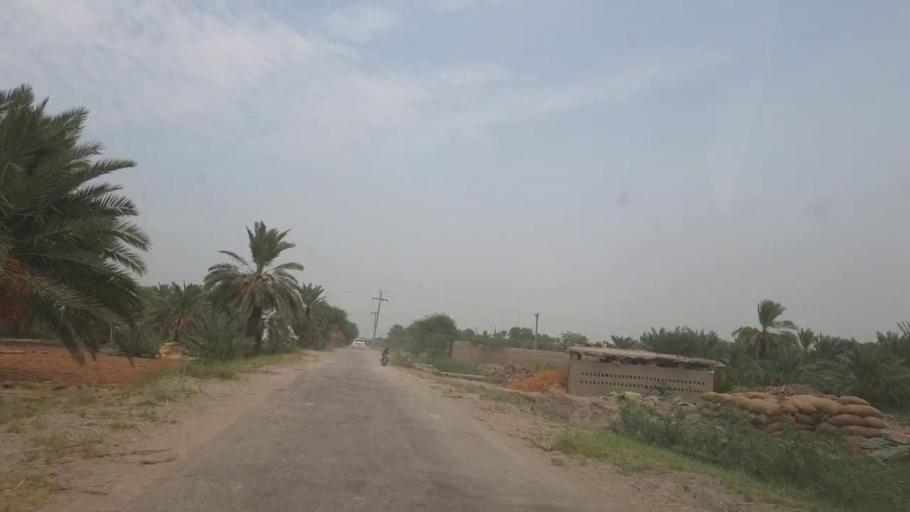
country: PK
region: Sindh
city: Kot Diji
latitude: 27.4317
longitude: 68.7046
